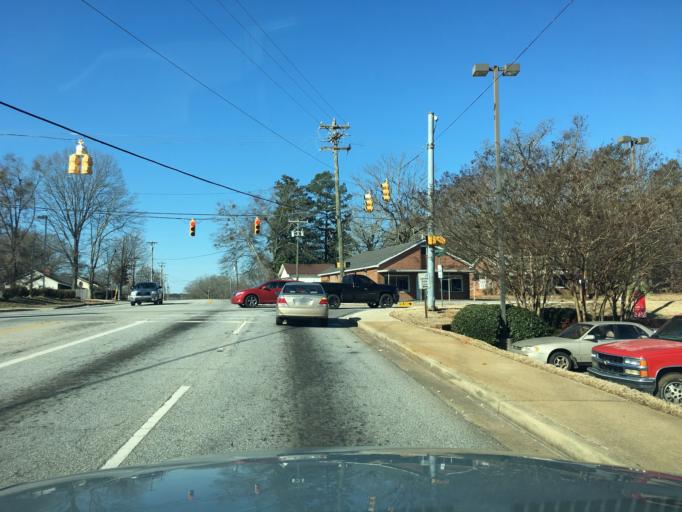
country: US
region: South Carolina
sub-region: Greenville County
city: Sans Souci
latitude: 34.8942
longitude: -82.4318
